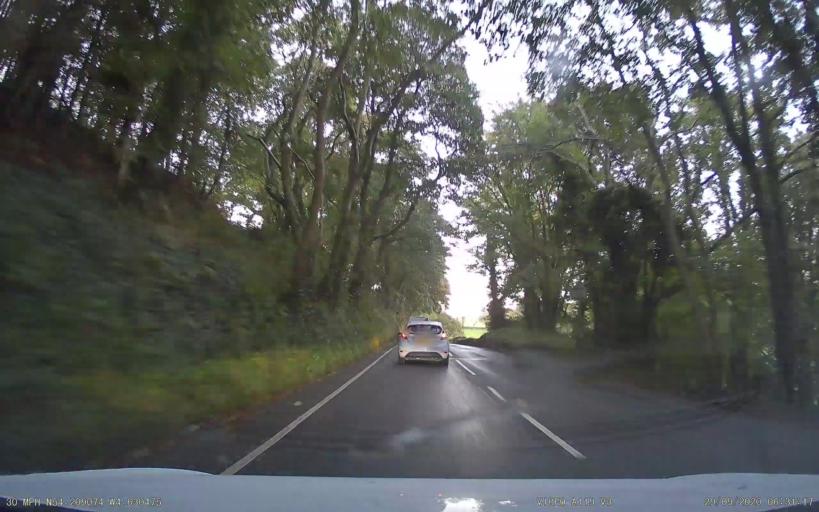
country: IM
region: Castletown
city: Castletown
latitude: 54.2091
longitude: -4.6305
